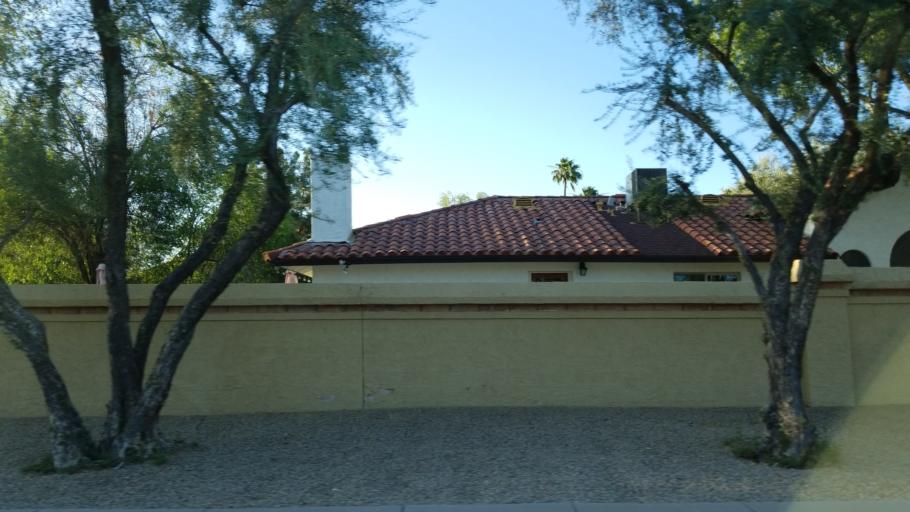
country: US
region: Arizona
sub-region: Maricopa County
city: Paradise Valley
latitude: 33.5785
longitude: -111.9125
